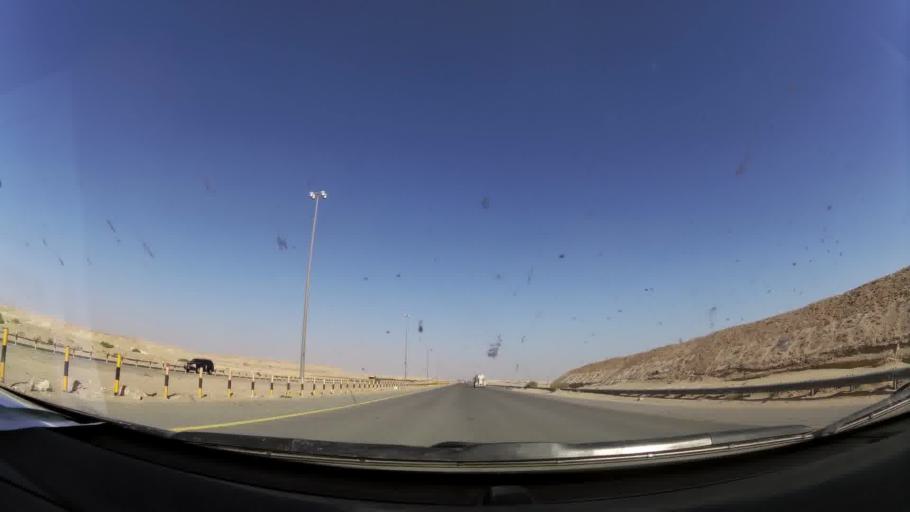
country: KW
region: Muhafazat al Jahra'
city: Al Jahra'
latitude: 29.4241
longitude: 47.7193
